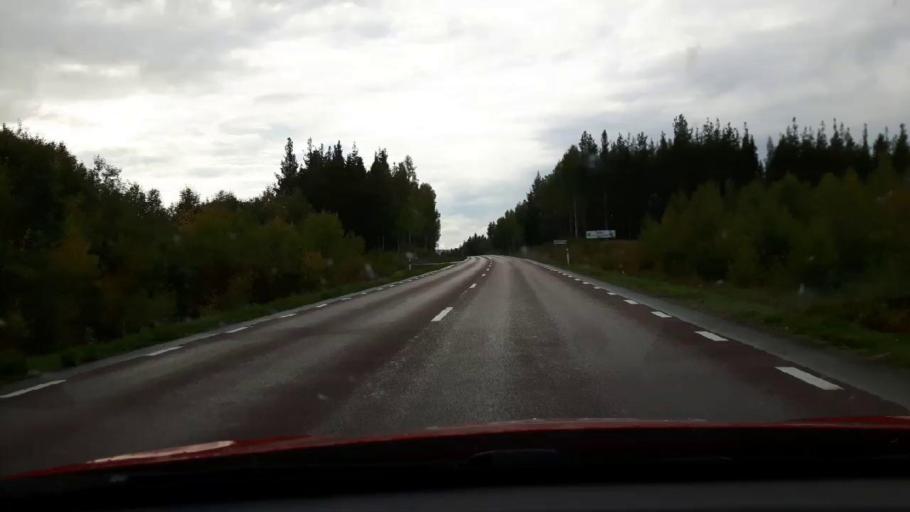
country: SE
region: Jaemtland
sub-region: Bergs Kommun
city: Hoverberg
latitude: 62.7921
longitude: 14.4754
